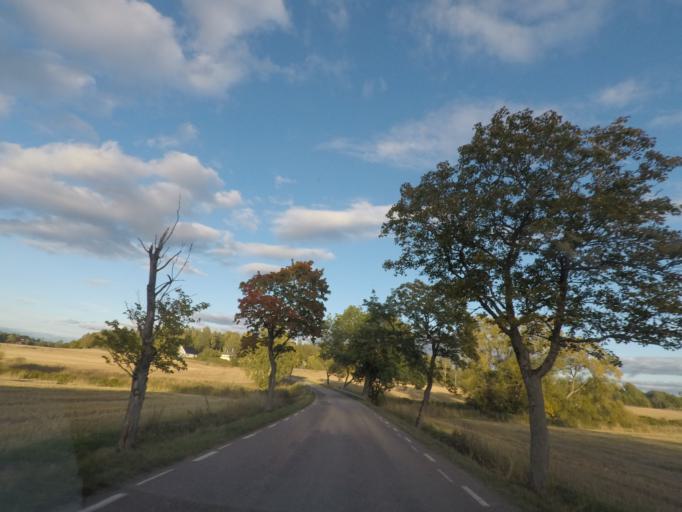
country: SE
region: Vaestmanland
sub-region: Kopings Kommun
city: Koping
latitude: 59.5093
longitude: 16.0694
